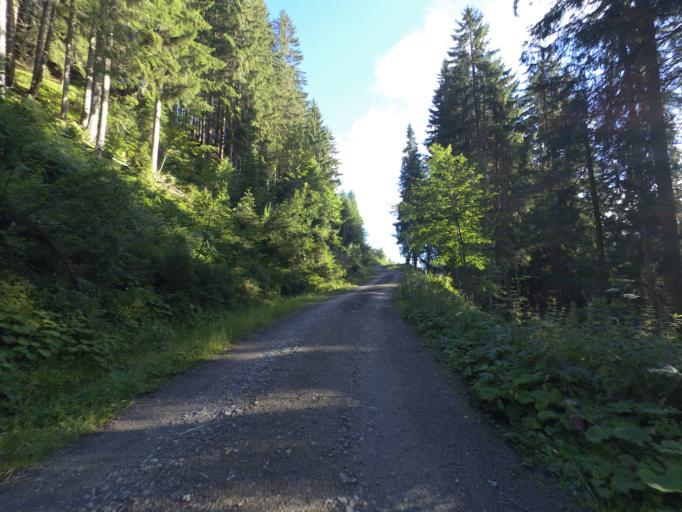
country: AT
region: Salzburg
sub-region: Politischer Bezirk Sankt Johann im Pongau
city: Goldegg
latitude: 47.3478
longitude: 13.1057
